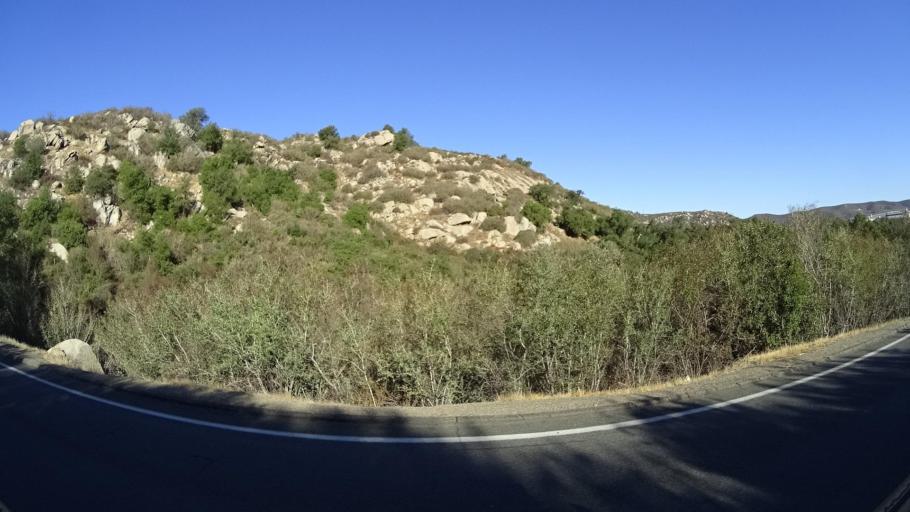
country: US
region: California
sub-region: San Diego County
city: Lakeside
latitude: 32.9275
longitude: -116.8735
